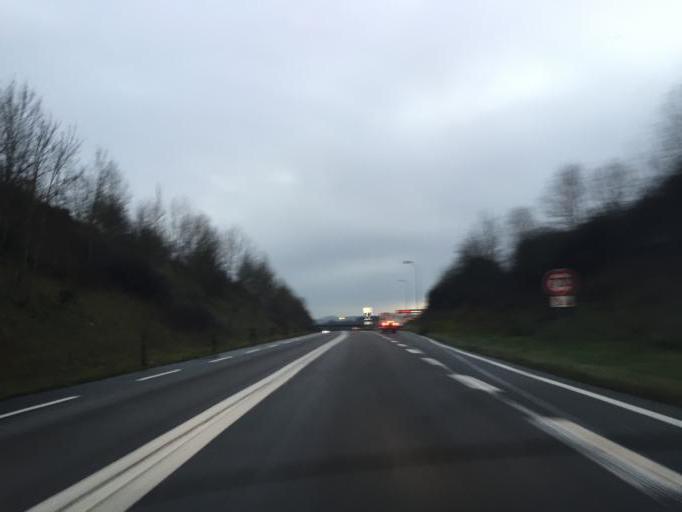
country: FR
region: Bourgogne
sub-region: Departement de Saone-et-Loire
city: Cluny
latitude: 46.3887
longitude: 4.6240
